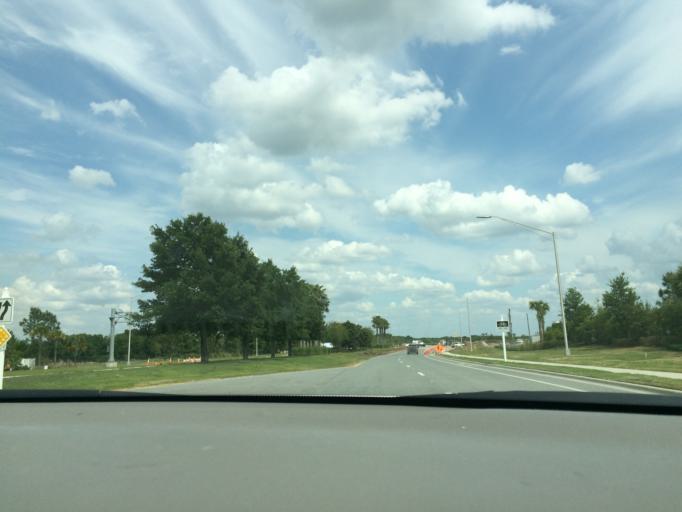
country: US
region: Florida
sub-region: Sarasota County
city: The Meadows
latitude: 27.4608
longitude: -82.4191
